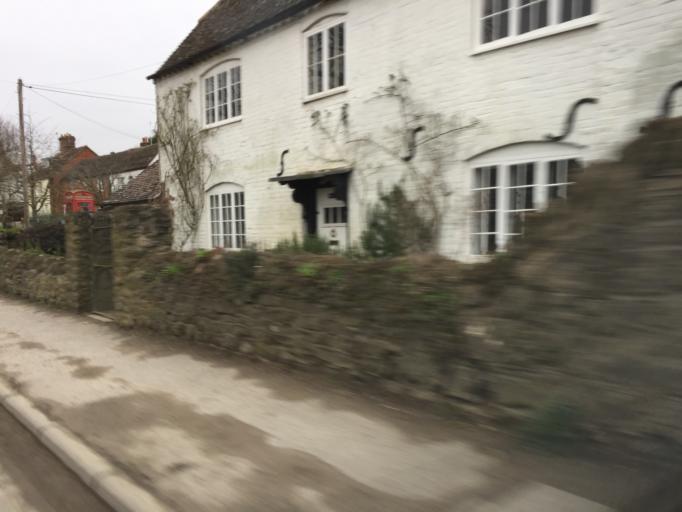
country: GB
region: England
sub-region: Oxfordshire
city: Wantage
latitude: 51.5923
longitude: -1.4523
